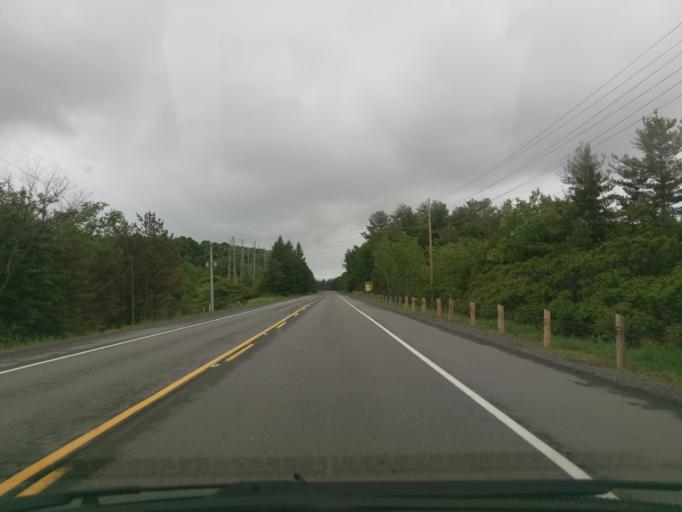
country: CA
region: Ontario
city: Clarence-Rockland
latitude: 45.5165
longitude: -75.4345
